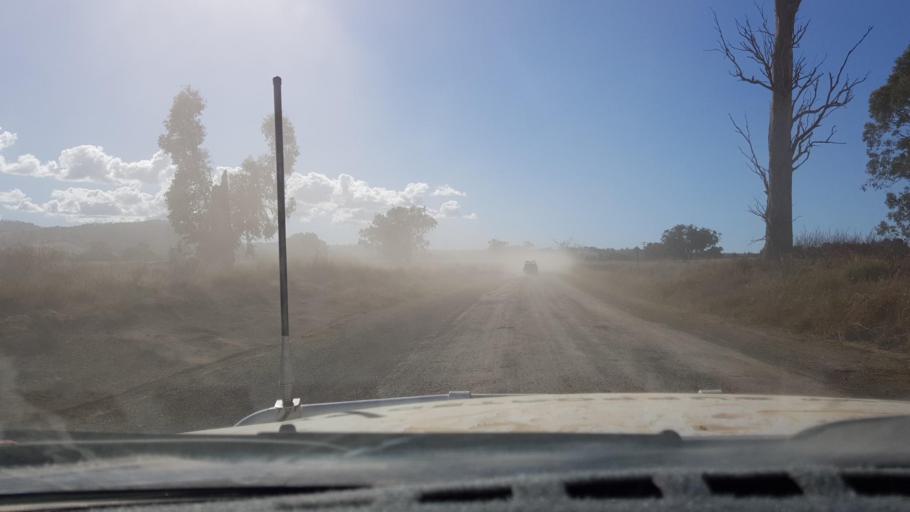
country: AU
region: New South Wales
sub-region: Narrabri
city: Blair Athol
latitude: -30.6730
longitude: 150.4500
